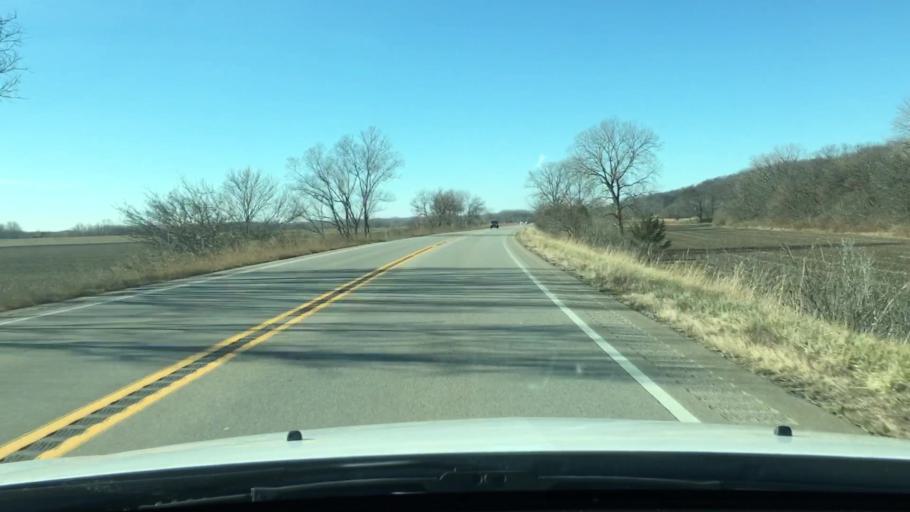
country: US
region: Illinois
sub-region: Peoria County
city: Glasford
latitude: 40.5525
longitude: -89.7950
